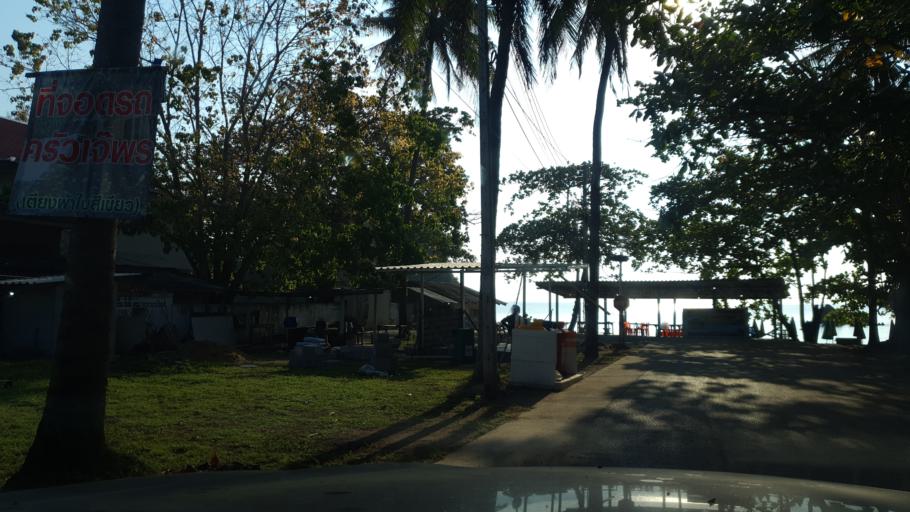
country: TH
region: Prachuap Khiri Khan
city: Bang Saphan
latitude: 11.2123
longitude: 99.5790
